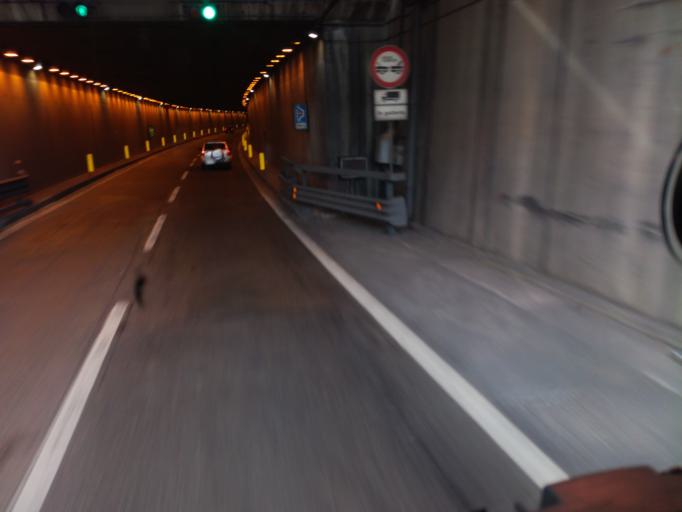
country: IT
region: Emilia-Romagna
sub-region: Forli-Cesena
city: Cesena
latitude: 44.1438
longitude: 12.2570
